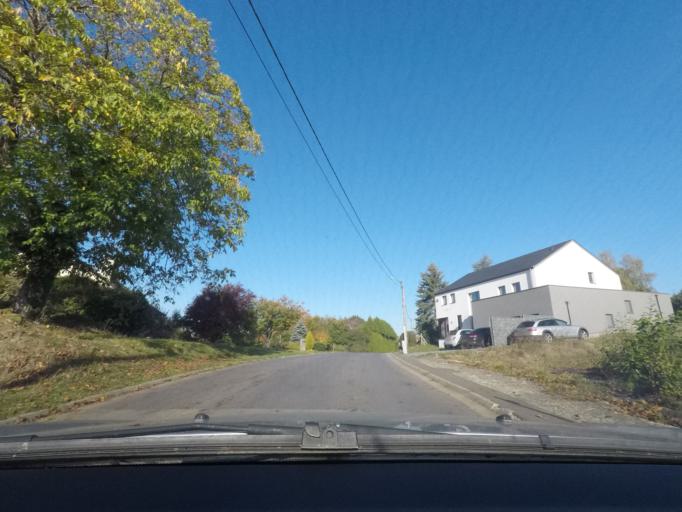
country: BE
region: Wallonia
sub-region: Province du Luxembourg
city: Messancy
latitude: 49.6365
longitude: 5.7968
